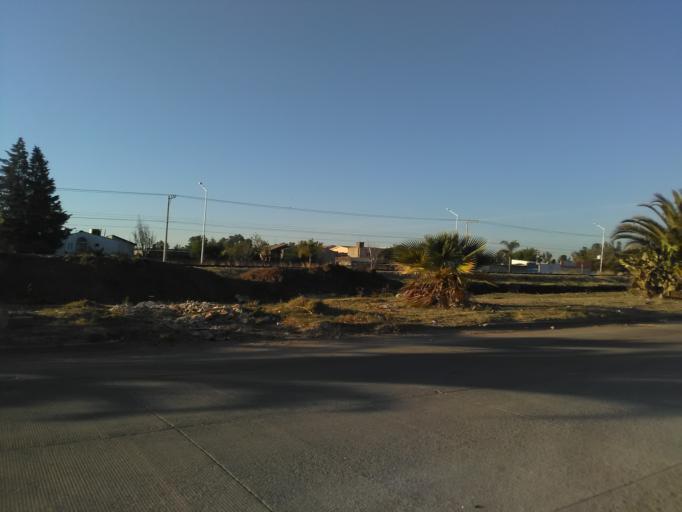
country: MX
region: Durango
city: Victoria de Durango
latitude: 24.0505
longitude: -104.6376
